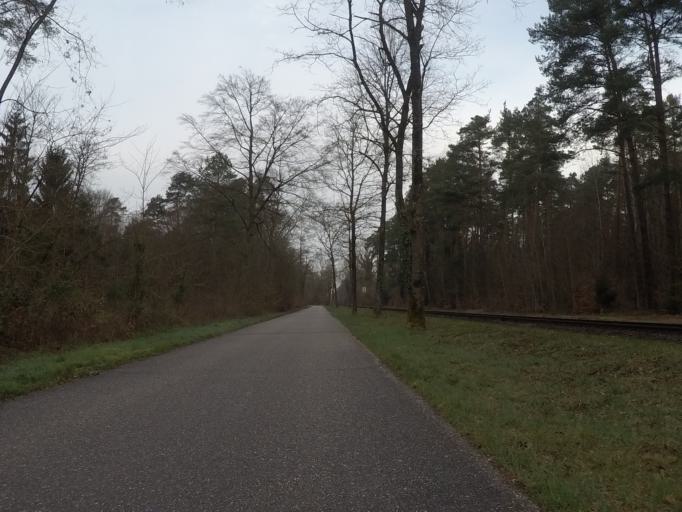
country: DE
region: Rheinland-Pfalz
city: Kandel
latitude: 49.0714
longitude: 8.2191
